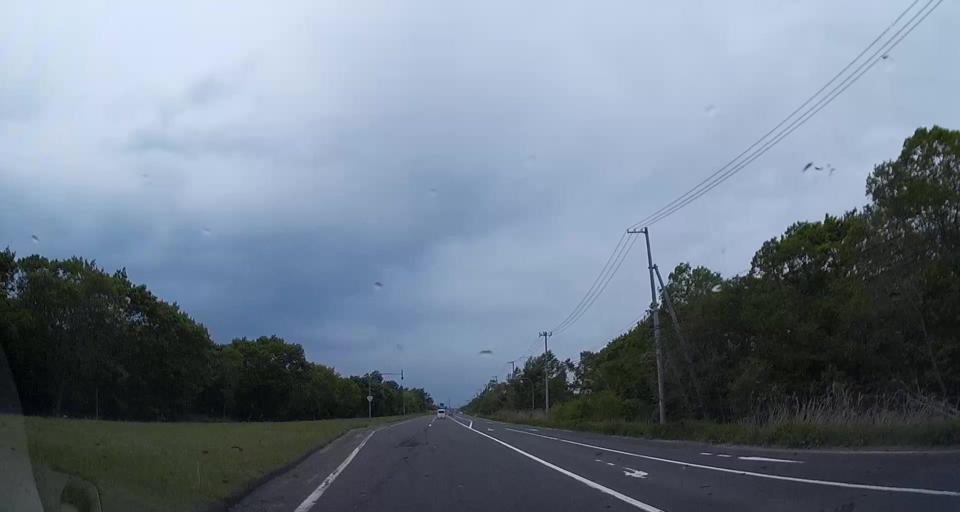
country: JP
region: Hokkaido
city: Tomakomai
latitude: 42.6853
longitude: 141.7224
